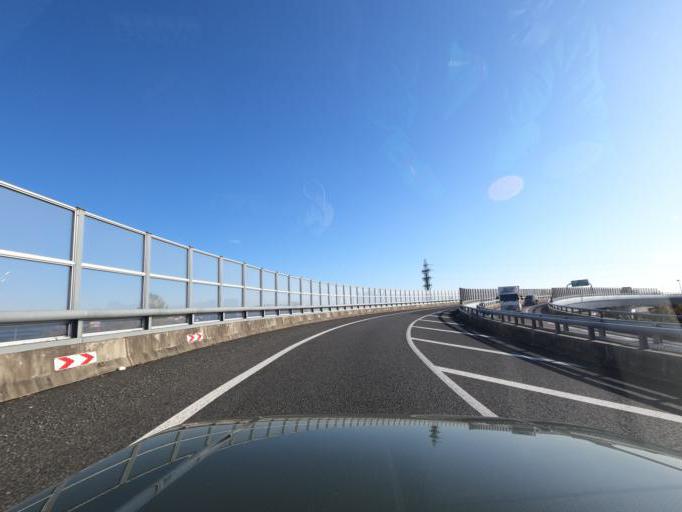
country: JP
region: Ibaraki
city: Naka
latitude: 36.0358
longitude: 140.1291
